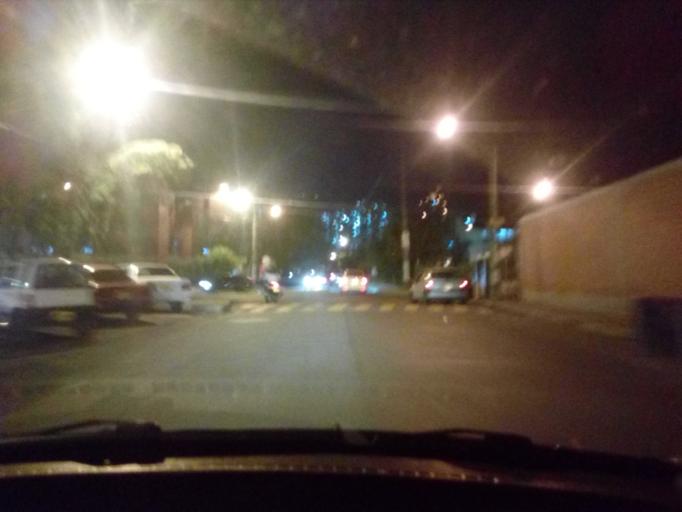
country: CO
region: Antioquia
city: Itagui
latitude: 6.1930
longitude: -75.5927
